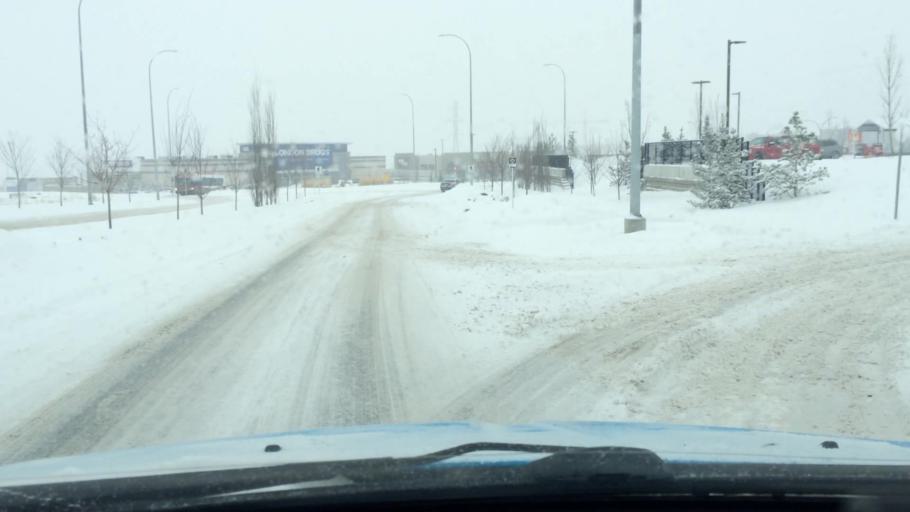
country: CA
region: Alberta
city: Calgary
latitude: 51.1704
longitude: -114.1512
